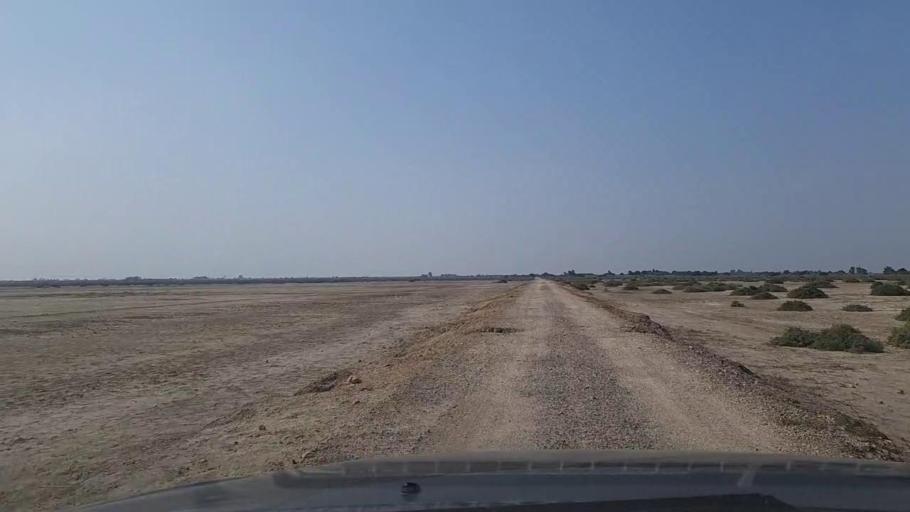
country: PK
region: Sindh
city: Mirpur Sakro
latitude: 24.4320
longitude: 67.7282
